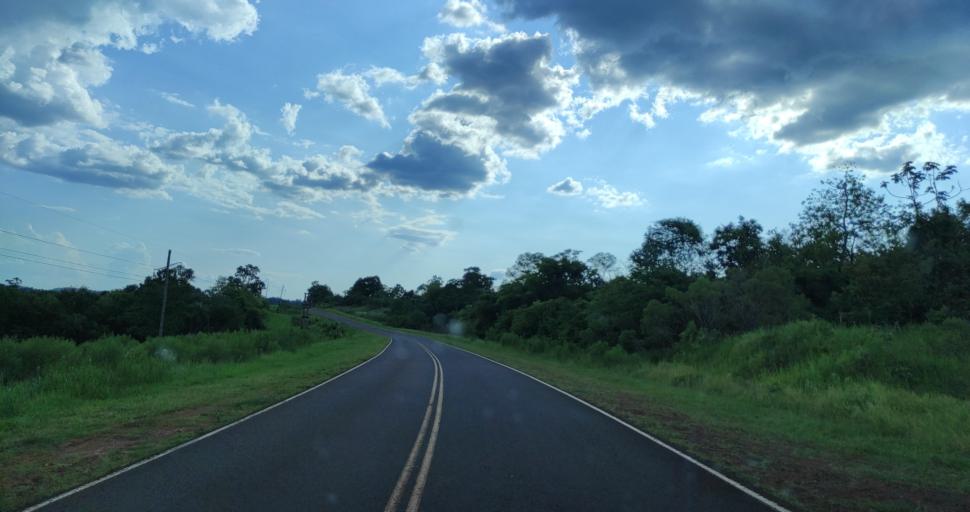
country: AR
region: Misiones
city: San Vicente
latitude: -26.3369
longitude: -54.1748
